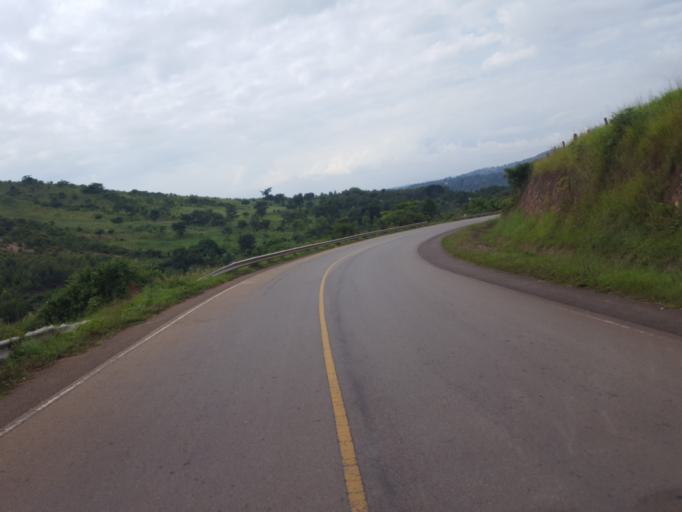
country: UG
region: Central Region
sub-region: Mityana District
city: Mityana
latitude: 0.6246
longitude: 32.1337
